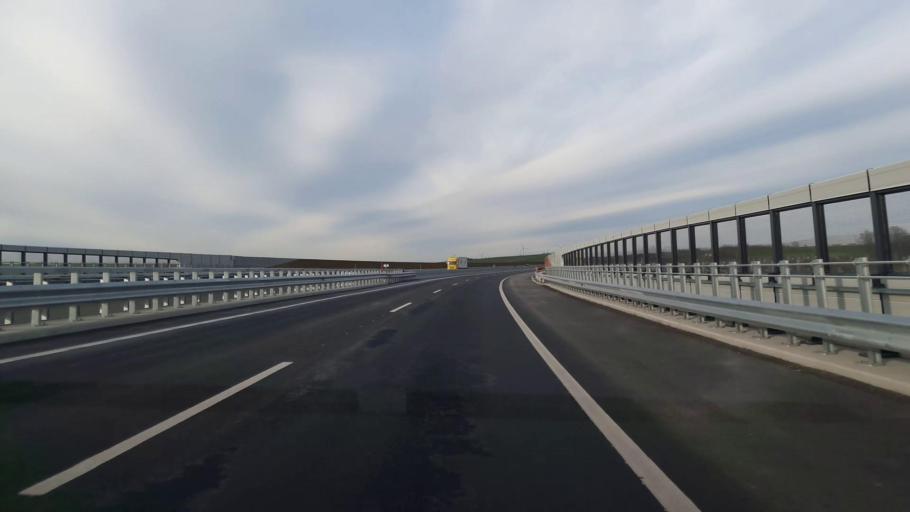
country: AT
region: Lower Austria
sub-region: Politischer Bezirk Mistelbach
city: Wilfersdorf
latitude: 48.5757
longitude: 16.6251
